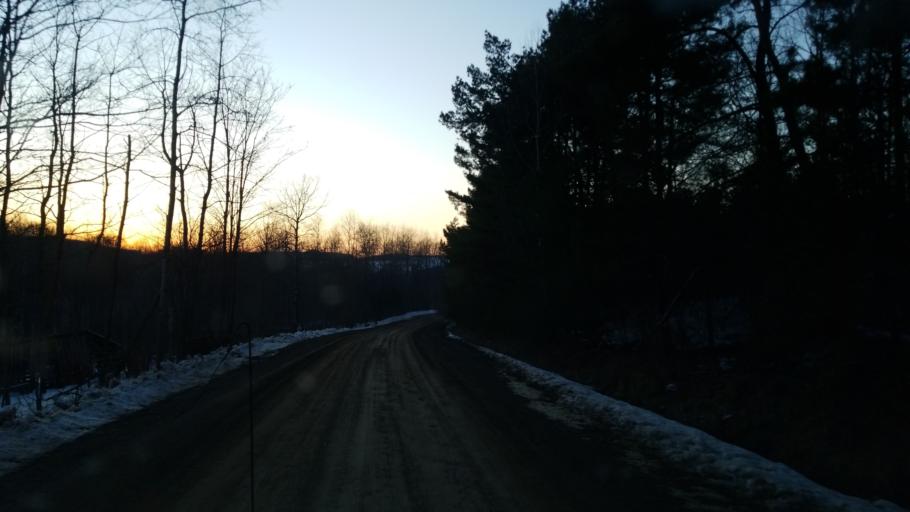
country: US
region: New York
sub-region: Allegany County
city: Andover
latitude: 42.0085
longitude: -77.7533
